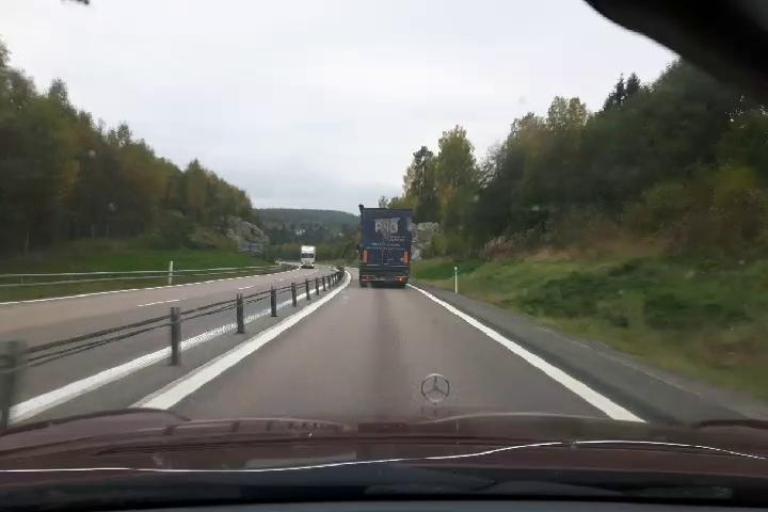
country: SE
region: Vaesternorrland
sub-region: Haernoesands Kommun
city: Haernoesand
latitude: 62.8364
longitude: 17.9687
